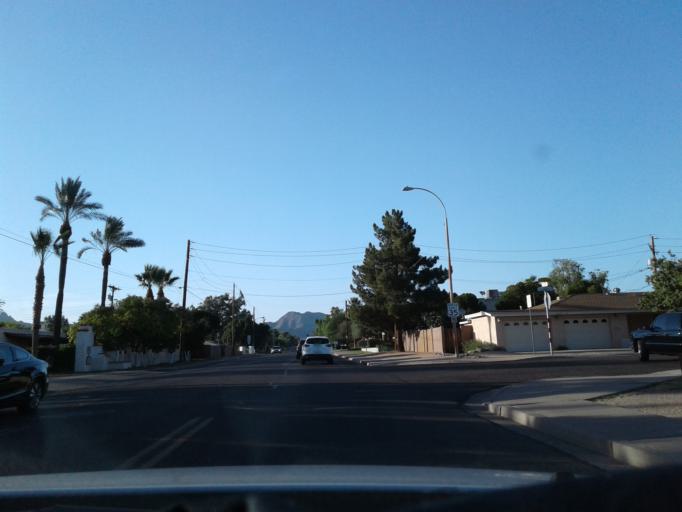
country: US
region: Arizona
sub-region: Maricopa County
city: Paradise Valley
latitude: 33.4999
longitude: -111.9954
